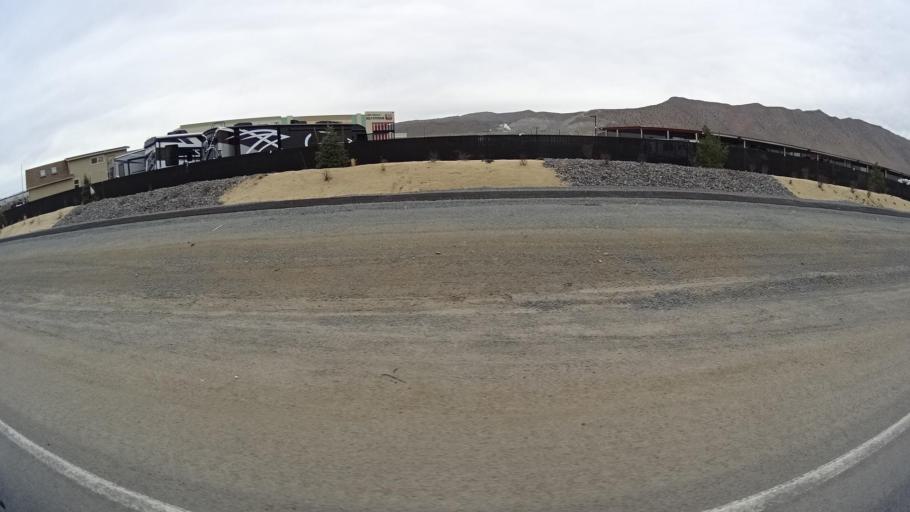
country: US
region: Nevada
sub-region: Washoe County
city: Spanish Springs
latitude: 39.6756
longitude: -119.7012
